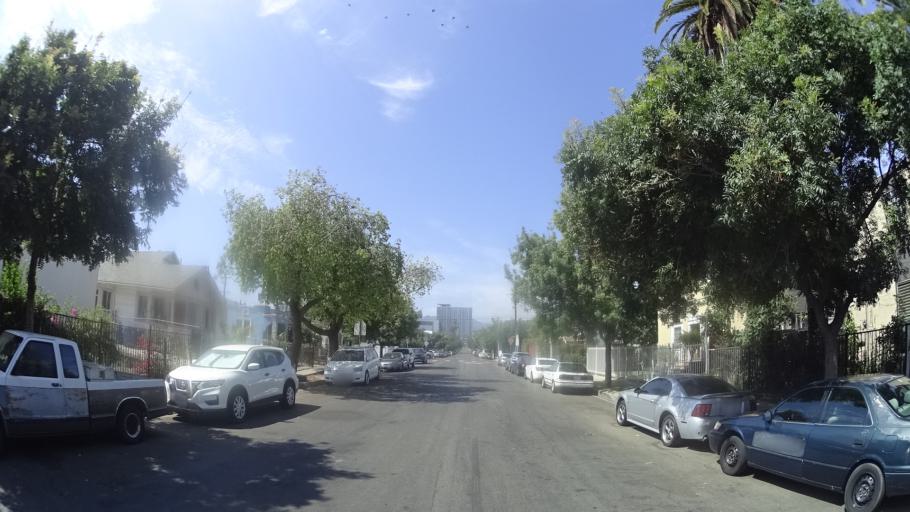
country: US
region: California
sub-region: Los Angeles County
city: Hollywood
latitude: 34.0920
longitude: -118.3190
